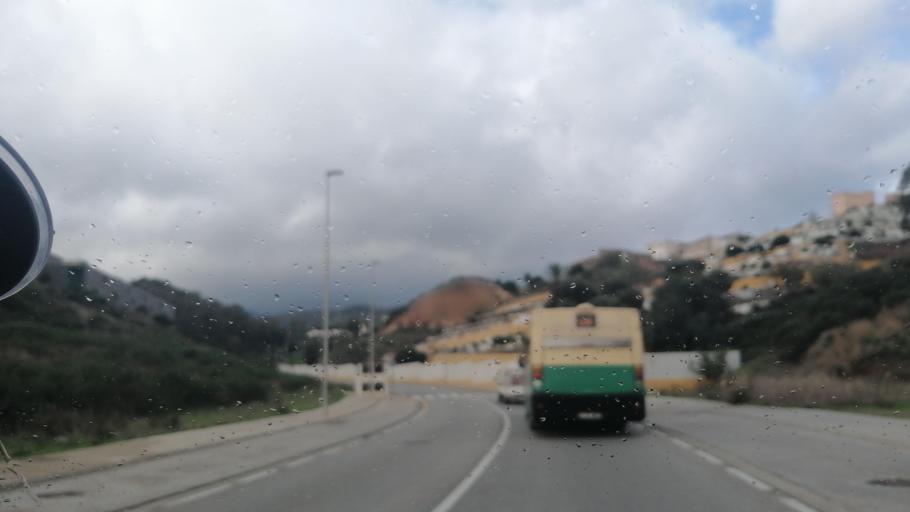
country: ES
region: Ceuta
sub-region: Ceuta
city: Ceuta
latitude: 35.8821
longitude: -5.3390
